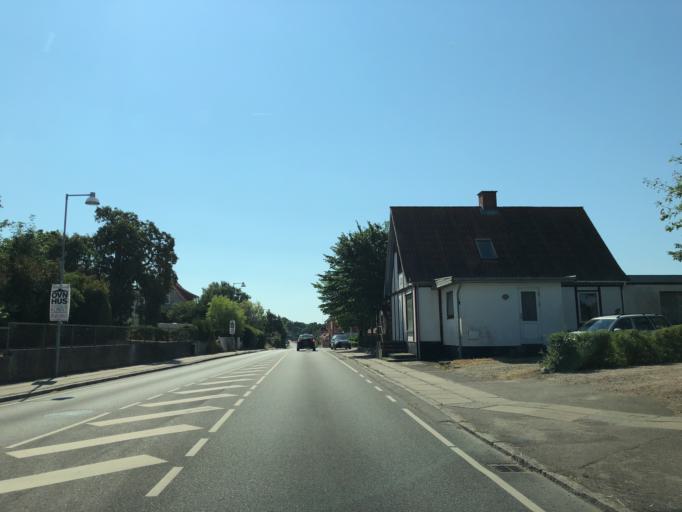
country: DK
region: Zealand
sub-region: Odsherred Kommune
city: Asnaes
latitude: 55.9682
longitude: 11.3642
